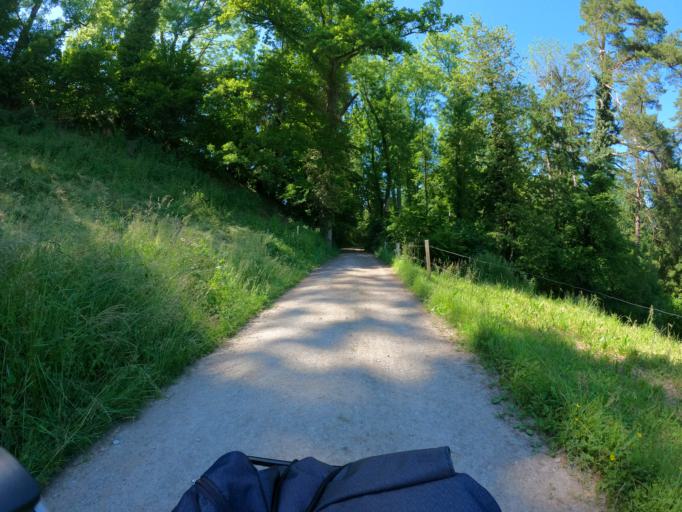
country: CH
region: Zurich
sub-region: Bezirk Affoltern
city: Affoltern / Sonnenberg
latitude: 47.2830
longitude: 8.4800
